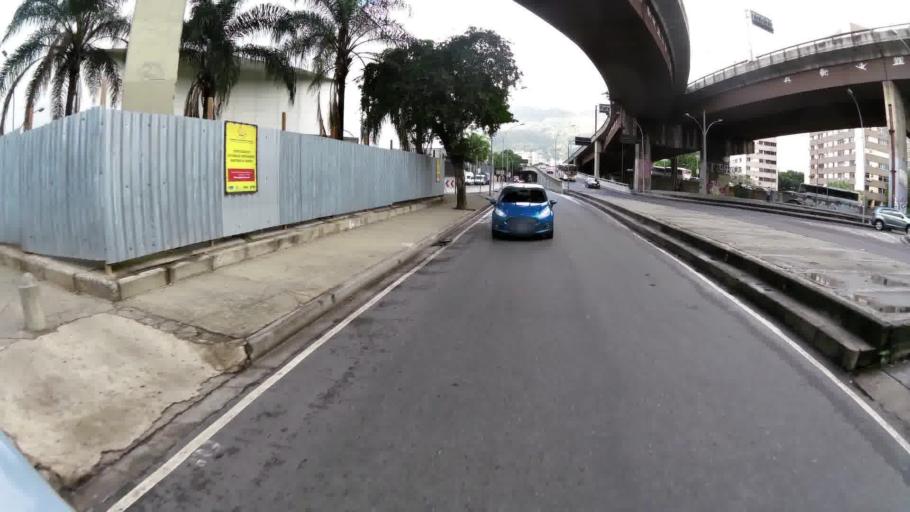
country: BR
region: Rio de Janeiro
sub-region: Rio De Janeiro
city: Rio de Janeiro
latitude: -22.9113
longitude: -43.2091
